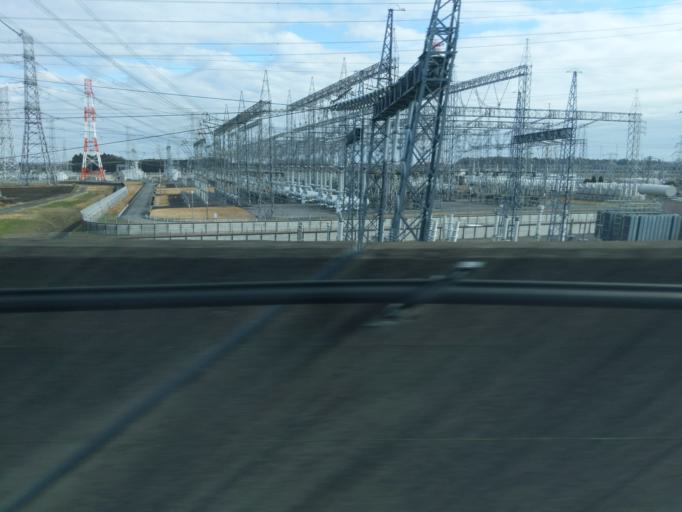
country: JP
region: Tochigi
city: Ujiie
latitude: 36.6558
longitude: 139.9132
